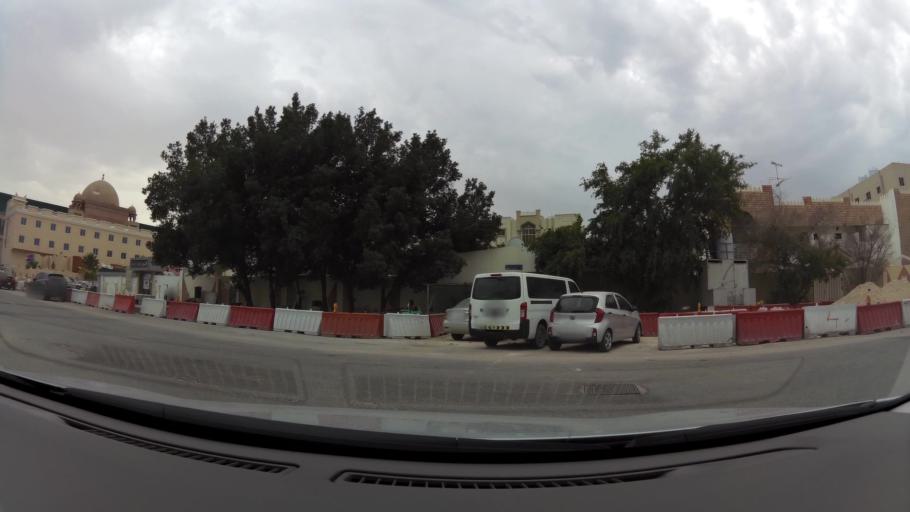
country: QA
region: Baladiyat ad Dawhah
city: Doha
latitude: 25.2750
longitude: 51.5022
